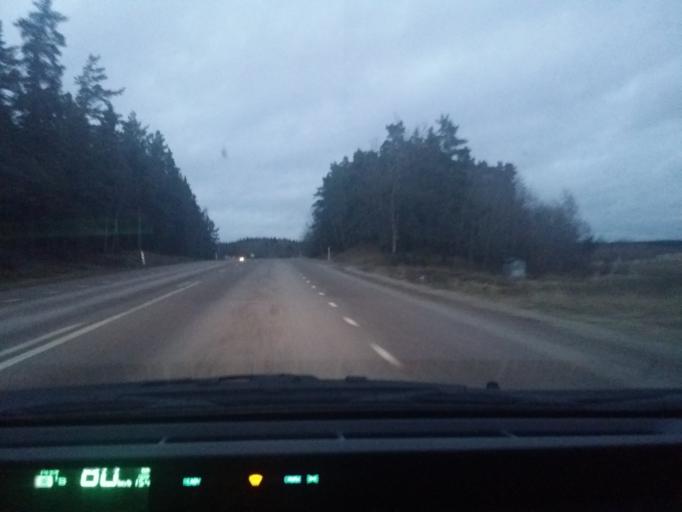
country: SE
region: Vaestmanland
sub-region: Hallstahammars Kommun
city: Kolback
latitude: 59.5705
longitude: 16.3509
